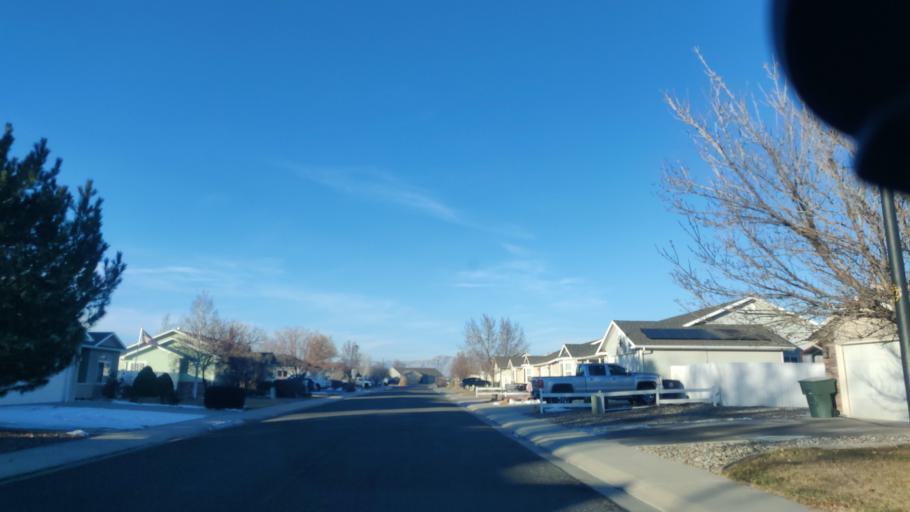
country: US
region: Colorado
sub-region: Mesa County
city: Grand Junction
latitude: 39.0603
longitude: -108.5241
